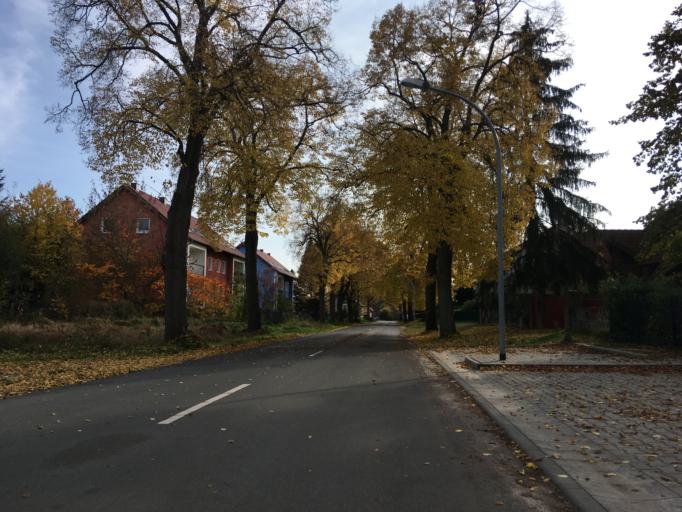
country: DE
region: Brandenburg
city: Marienwerder
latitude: 52.9100
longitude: 13.5286
